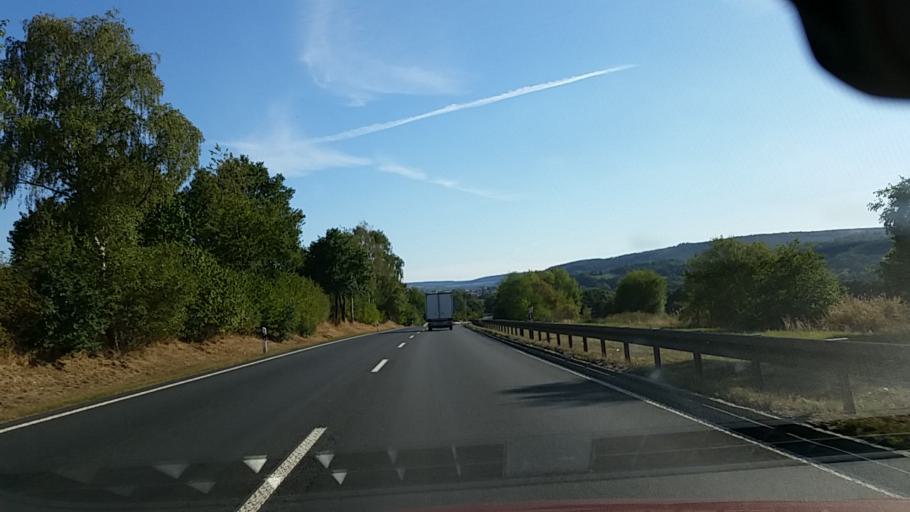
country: DE
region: Thuringia
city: Fambach
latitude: 50.7501
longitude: 10.3570
